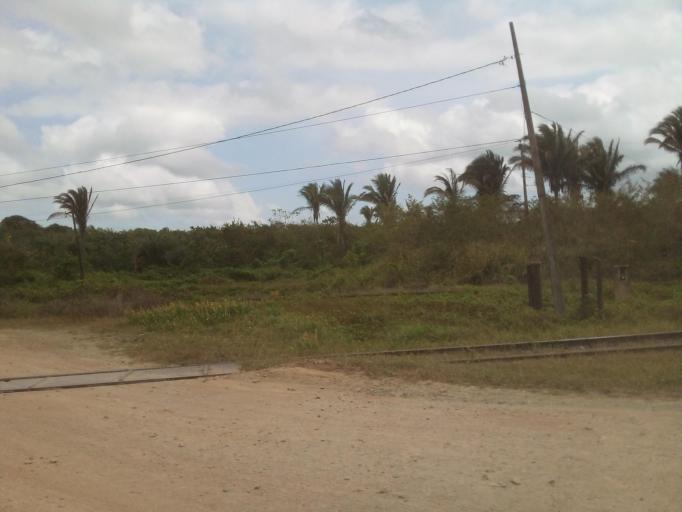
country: BR
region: Maranhao
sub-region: Icatu
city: Icatu
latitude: -2.9272
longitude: -44.3462
